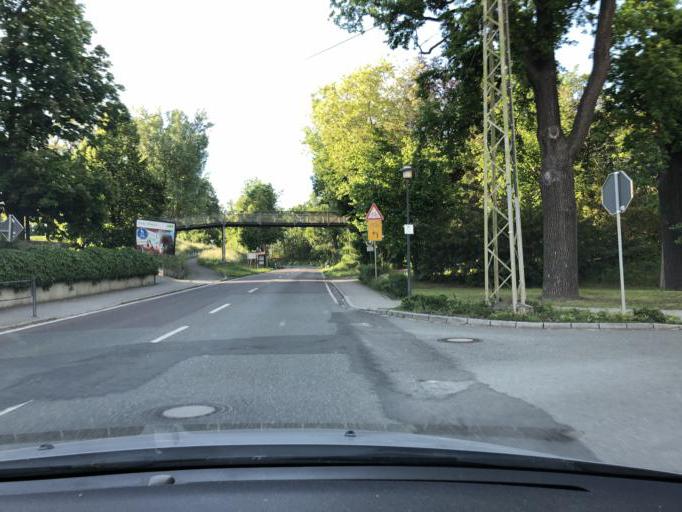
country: DE
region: Thuringia
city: Rositz
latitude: 51.0185
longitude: 12.3679
